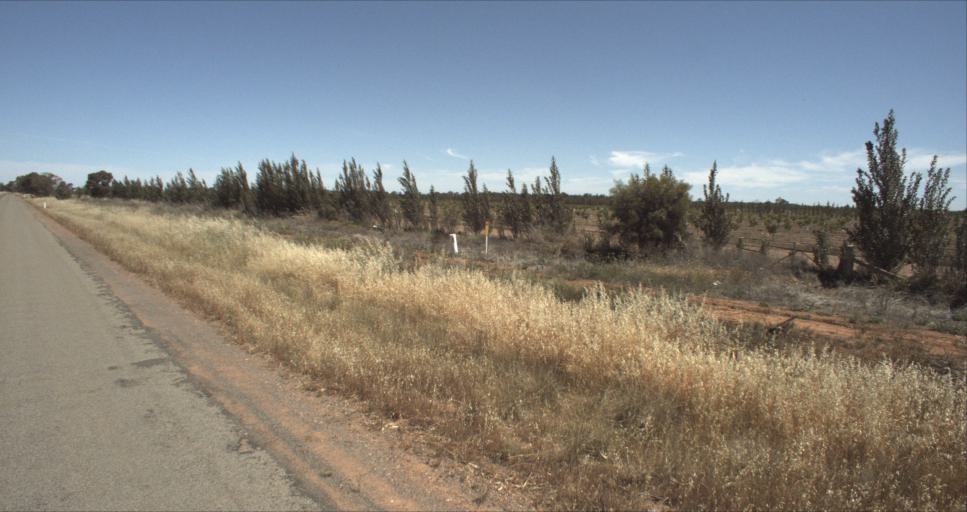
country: AU
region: New South Wales
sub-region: Leeton
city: Leeton
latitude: -34.5136
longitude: 146.3451
